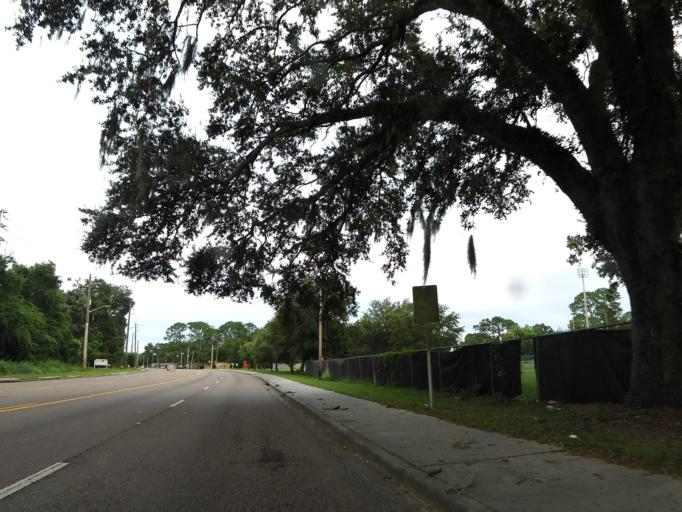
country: US
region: Florida
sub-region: Duval County
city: Jacksonville
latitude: 30.3839
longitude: -81.7077
